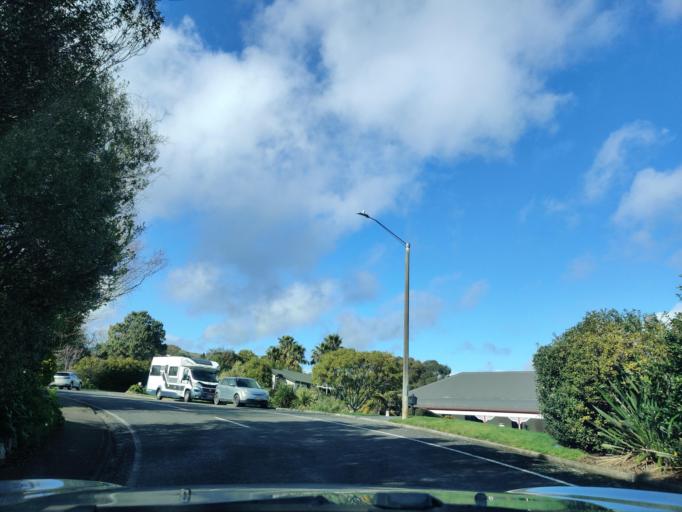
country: NZ
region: Hawke's Bay
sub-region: Hastings District
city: Hastings
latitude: -39.6741
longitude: 176.8948
